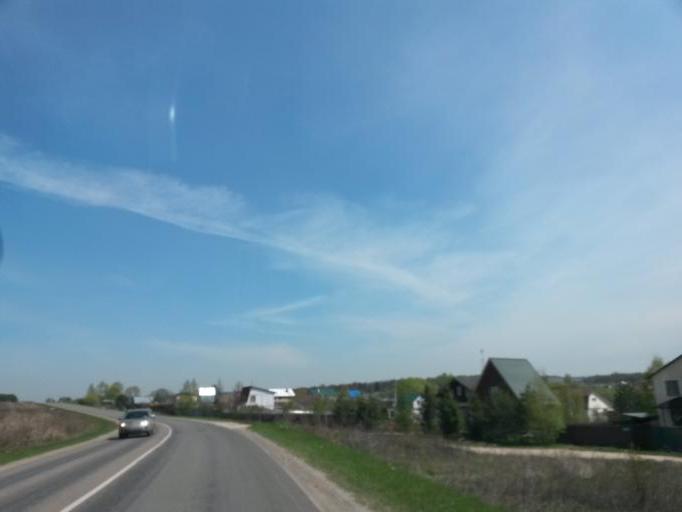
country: RU
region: Moskovskaya
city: Lyubuchany
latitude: 55.2864
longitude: 37.6235
